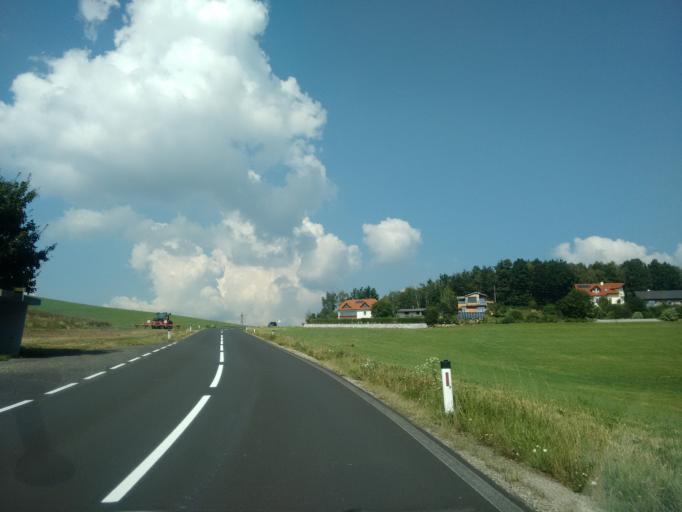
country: AT
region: Upper Austria
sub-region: Politischer Bezirk Urfahr-Umgebung
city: Altenberg bei Linz
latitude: 48.3948
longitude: 14.3468
